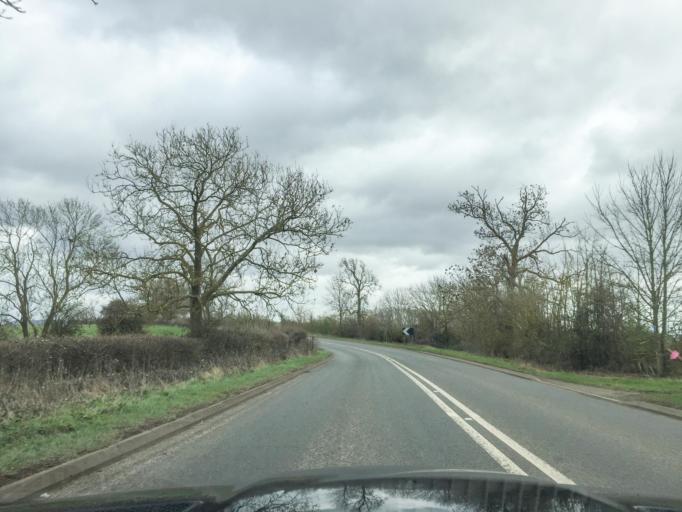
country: GB
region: England
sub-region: Warwickshire
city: Wellesbourne Mountford
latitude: 52.1238
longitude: -1.5565
